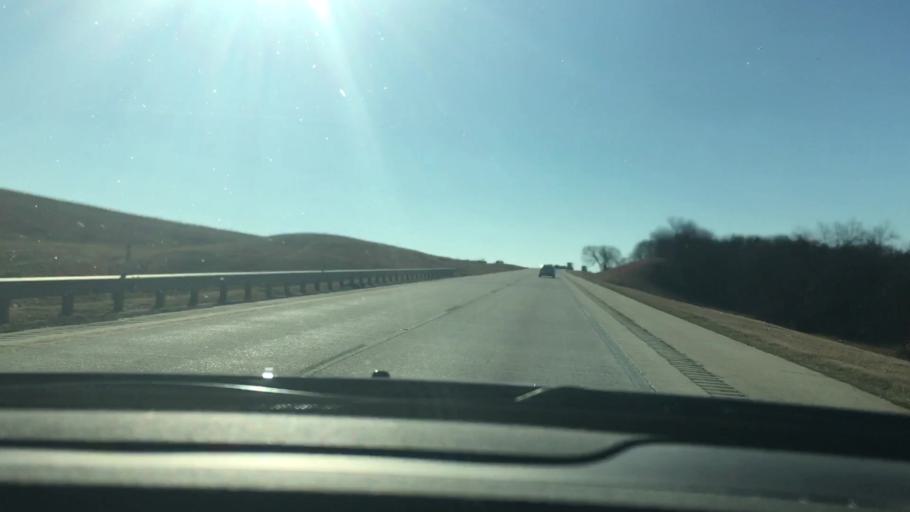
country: US
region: Oklahoma
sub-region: Love County
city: Marietta
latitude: 33.9857
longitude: -97.1375
